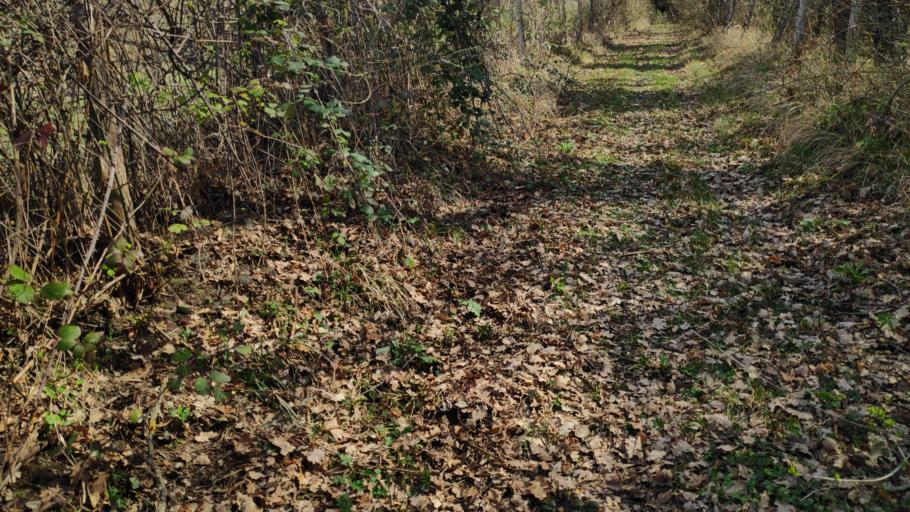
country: IT
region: Emilia-Romagna
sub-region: Provincia di Bologna
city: Berzantina
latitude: 44.1751
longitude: 10.9908
